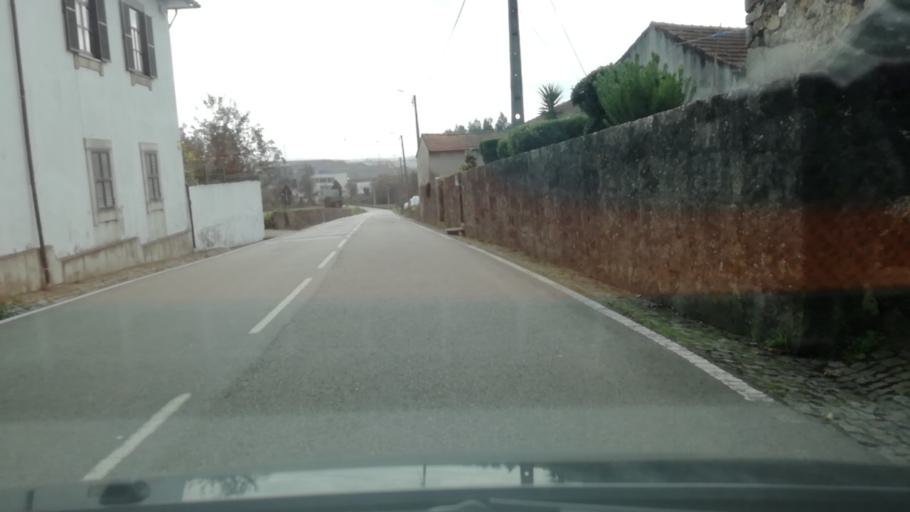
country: PT
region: Porto
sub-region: Maia
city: Maia
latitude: 41.2463
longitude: -8.6363
